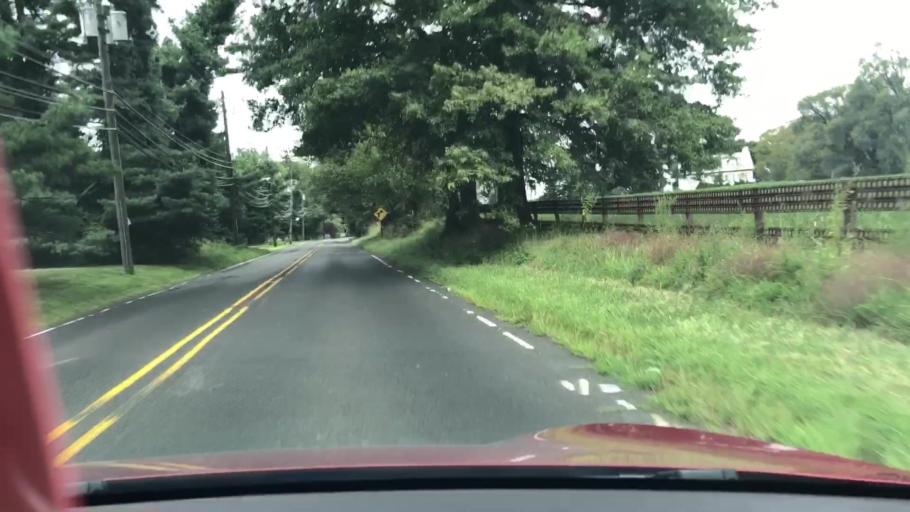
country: US
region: New Jersey
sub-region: Monmouth County
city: Allentown
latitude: 40.1829
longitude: -74.5911
